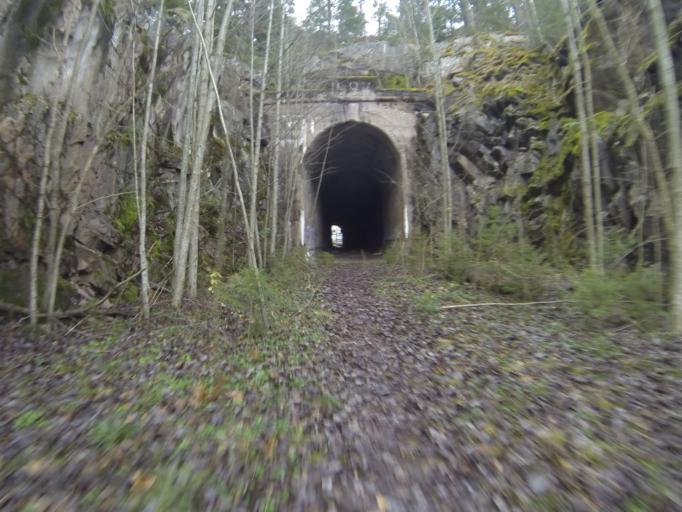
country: FI
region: Varsinais-Suomi
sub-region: Salo
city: Halikko
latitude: 60.4018
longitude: 23.0176
